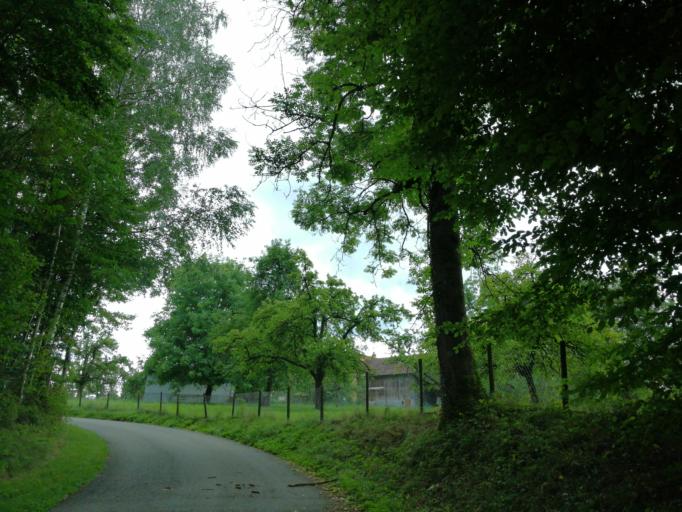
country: CH
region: Thurgau
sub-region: Weinfelden District
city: Sulgen
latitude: 47.5145
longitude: 9.1870
